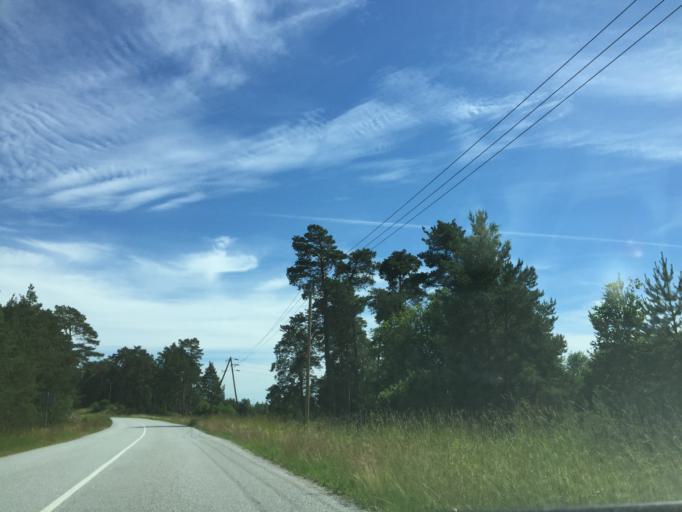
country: LV
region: Rojas
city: Roja
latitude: 57.5765
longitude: 22.6279
